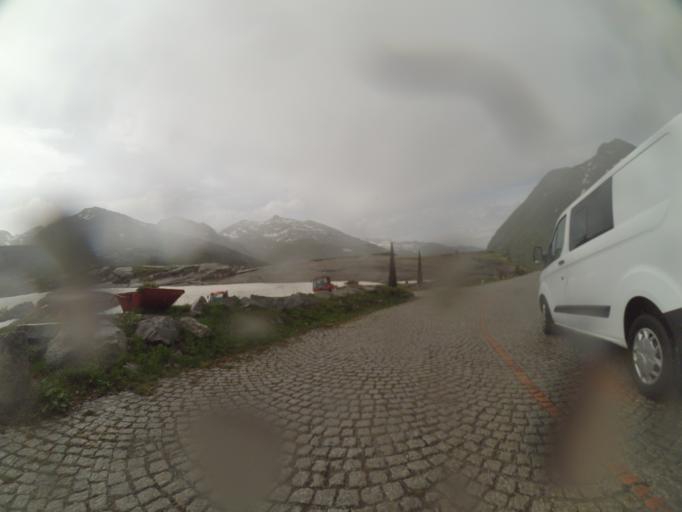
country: CH
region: Ticino
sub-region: Leventina District
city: Airolo
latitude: 46.5623
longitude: 8.5564
